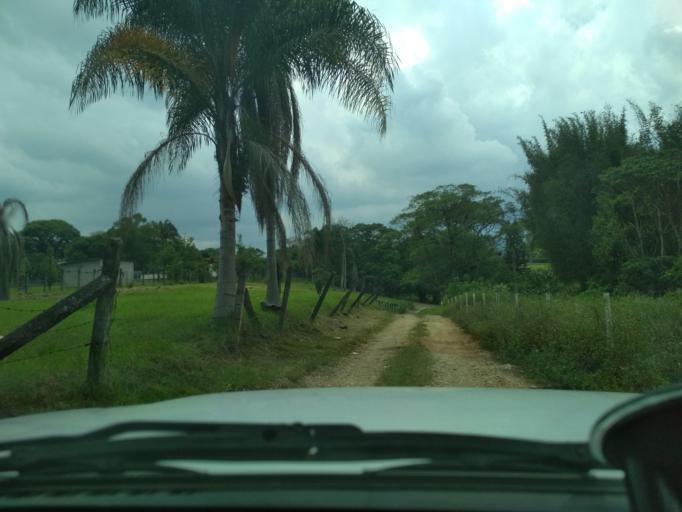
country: MX
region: Veracruz
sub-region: Cordoba
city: San Jose de Abajo [Unidad Habitacional]
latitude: 18.9186
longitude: -96.9553
